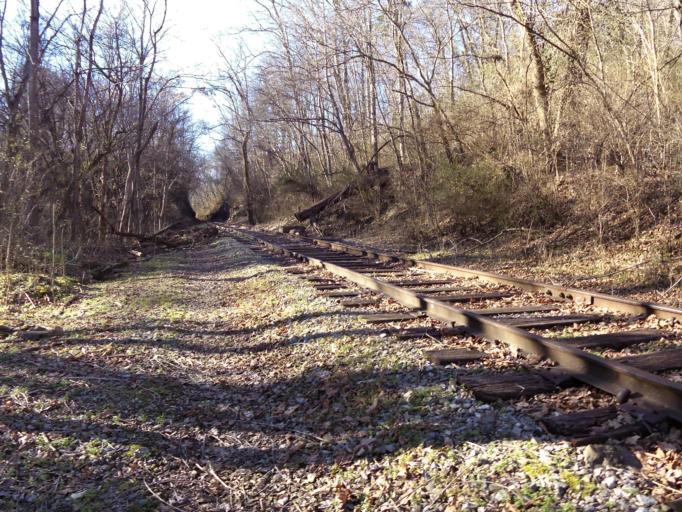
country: US
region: Tennessee
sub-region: Knox County
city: Knoxville
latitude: 35.9491
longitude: -83.8723
